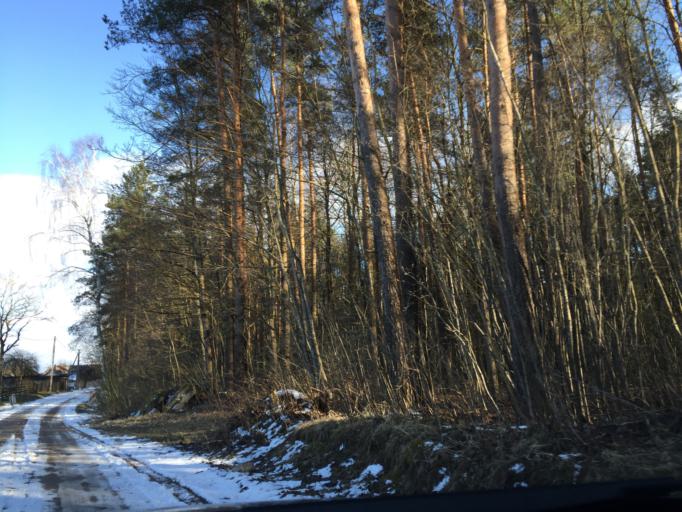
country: LV
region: Kekava
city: Kekava
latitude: 56.8466
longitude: 24.1891
